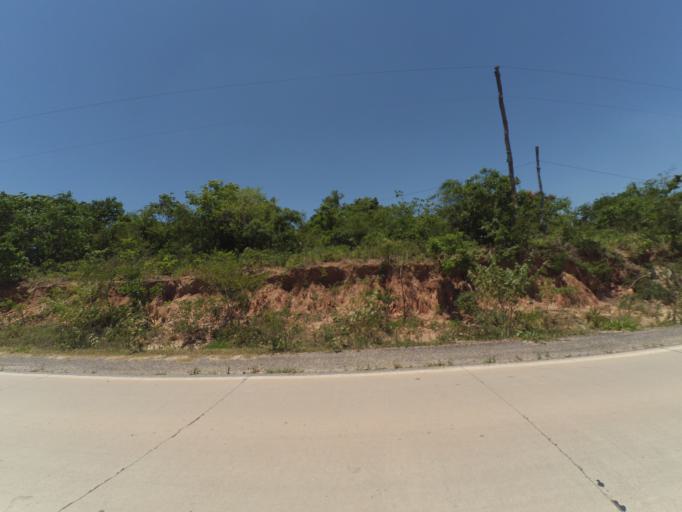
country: BO
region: Santa Cruz
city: Santa Cruz de la Sierra
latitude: -17.8219
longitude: -63.2883
